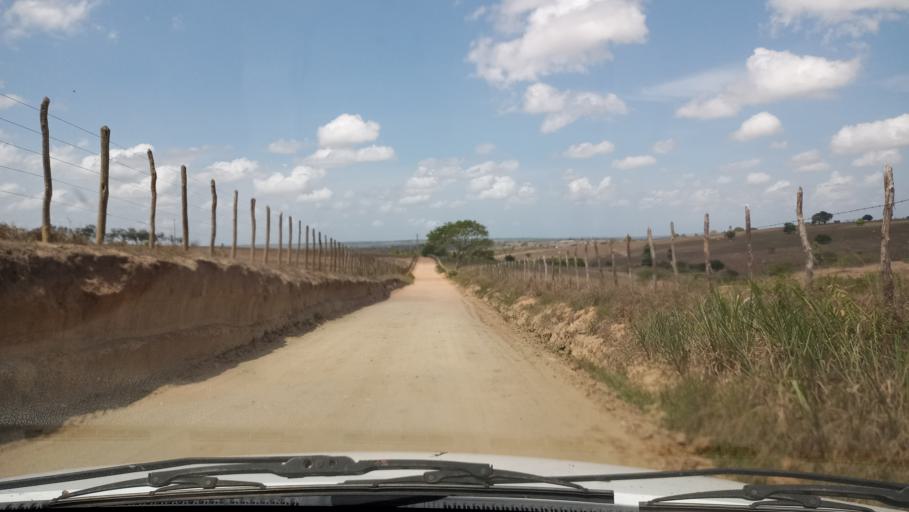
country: BR
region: Rio Grande do Norte
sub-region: Goianinha
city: Goianinha
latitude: -6.3461
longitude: -35.3294
